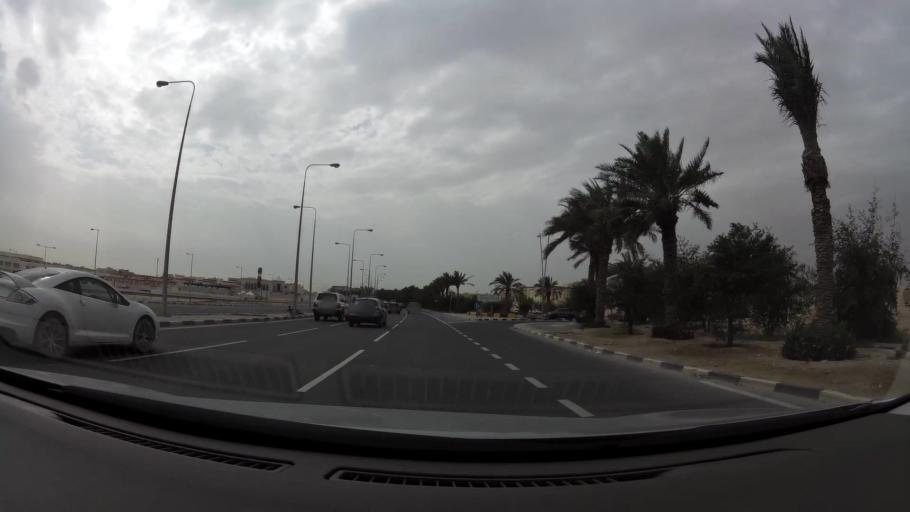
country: QA
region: Baladiyat ad Dawhah
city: Doha
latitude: 25.3346
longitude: 51.4947
